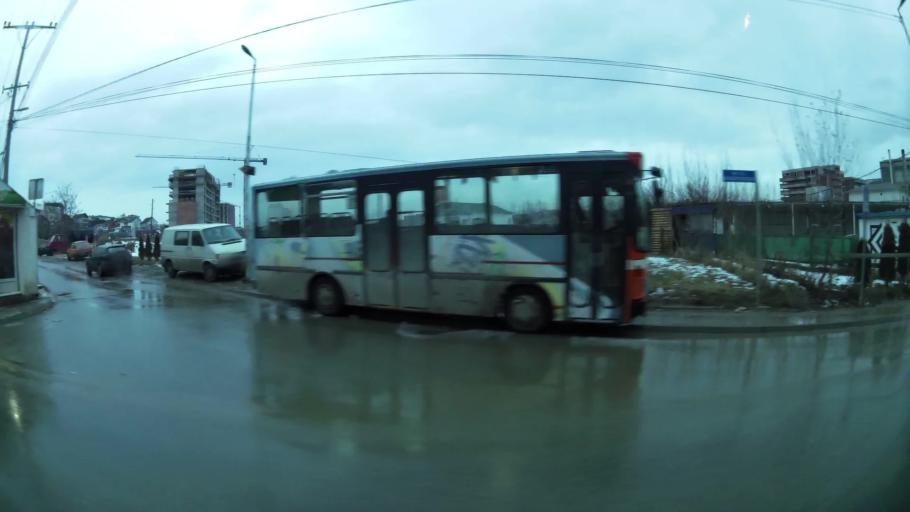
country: XK
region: Pristina
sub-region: Komuna e Prishtines
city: Pristina
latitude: 42.6408
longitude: 21.1637
